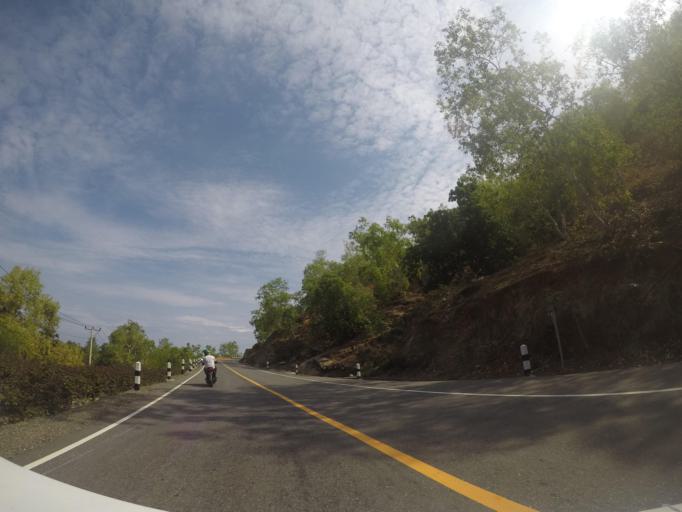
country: TL
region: Manatuto
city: Manatuto
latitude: -8.4782
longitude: 125.8931
